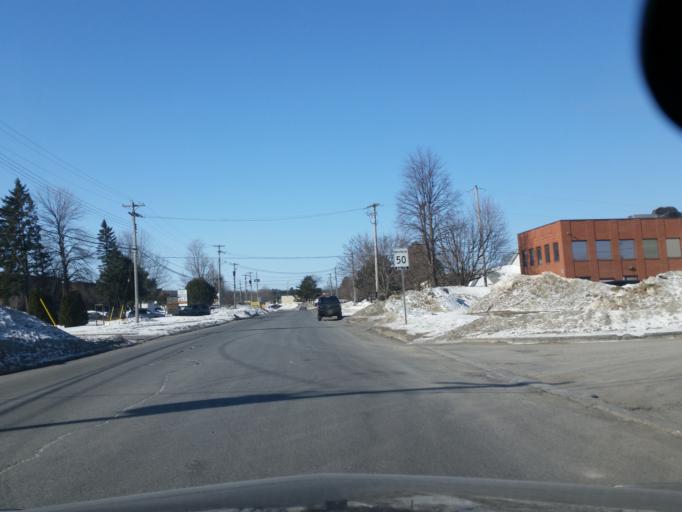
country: CA
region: Ontario
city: Ottawa
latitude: 45.3336
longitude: -75.7176
